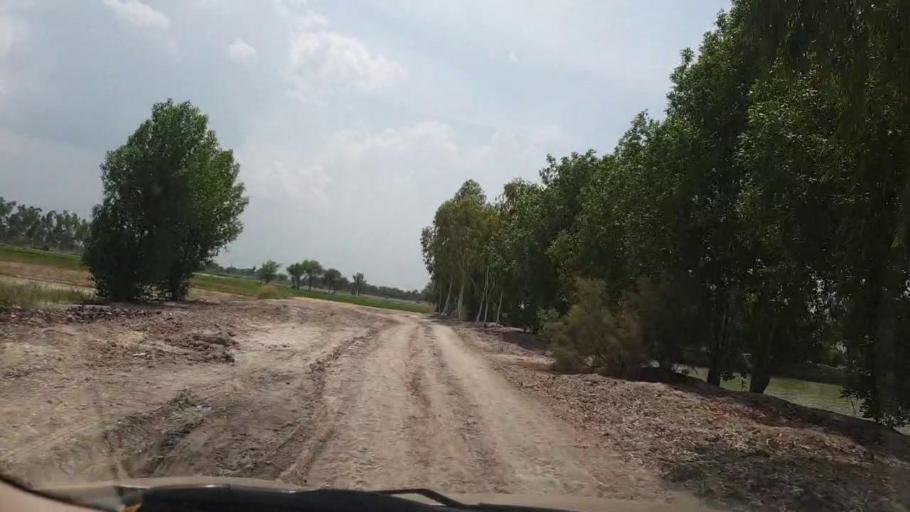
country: PK
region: Sindh
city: Larkana
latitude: 27.6152
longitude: 68.1543
